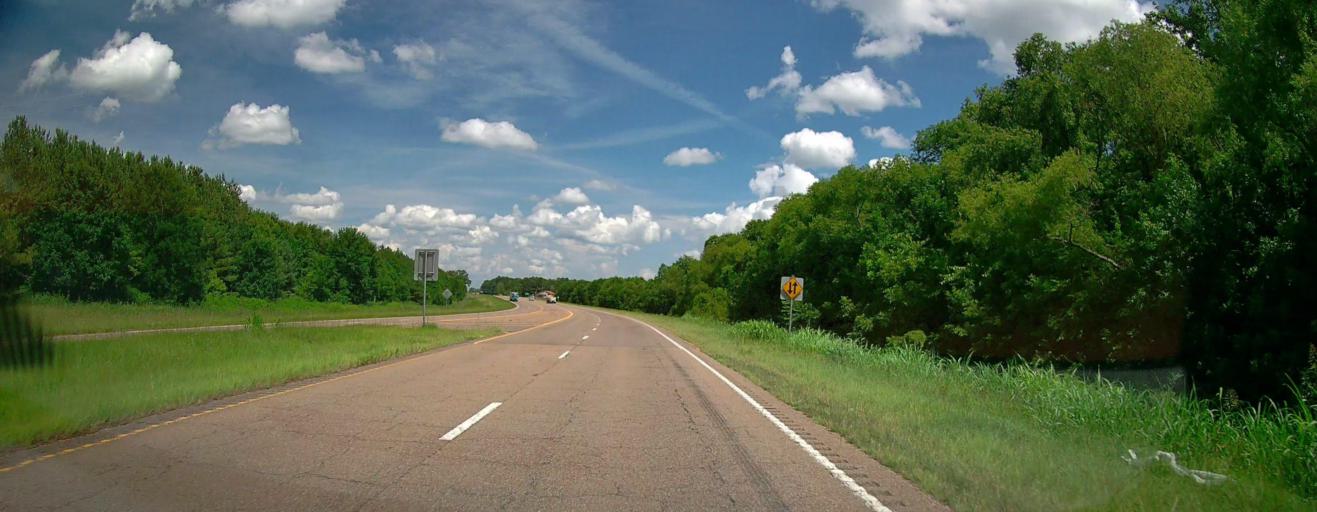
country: US
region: Mississippi
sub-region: Monroe County
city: Aberdeen
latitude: 33.8152
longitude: -88.5735
